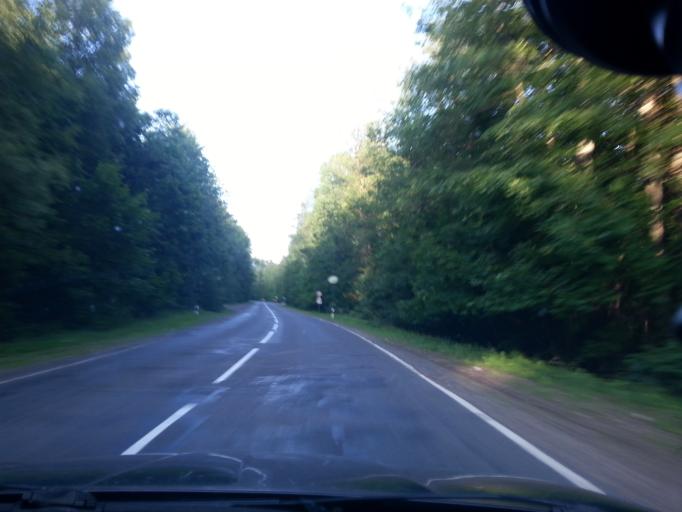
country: BY
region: Minsk
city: Svir
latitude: 54.9218
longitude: 26.5201
